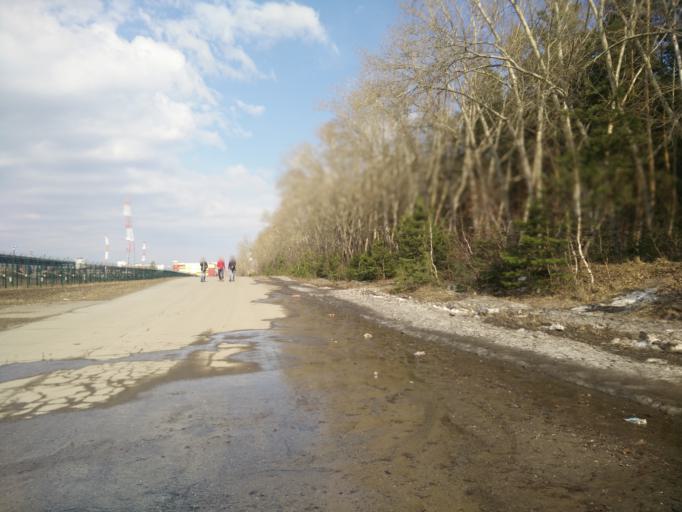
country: RU
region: Novosibirsk
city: Berdsk
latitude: 54.7615
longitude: 83.0724
